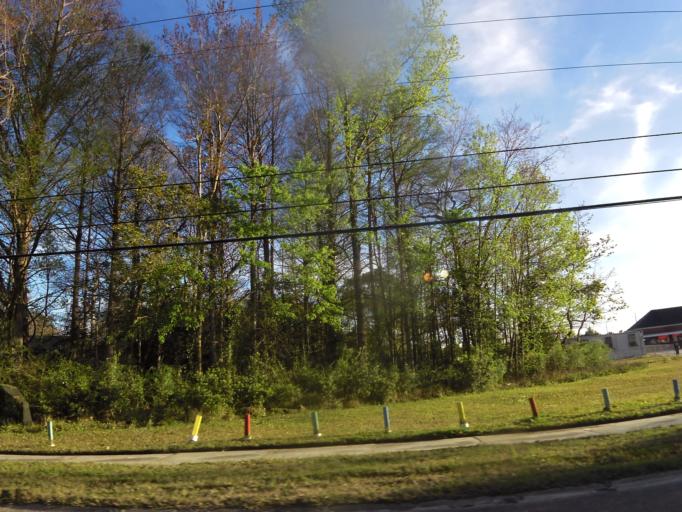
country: US
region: Florida
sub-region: Duval County
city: Jacksonville
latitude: 30.4413
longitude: -81.6399
